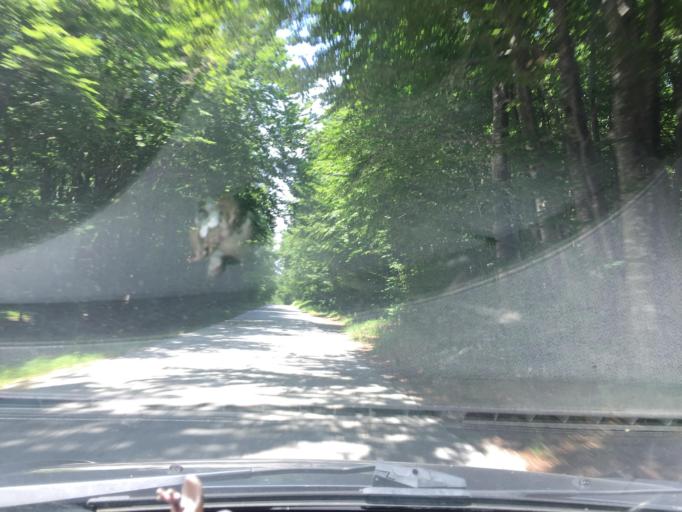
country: HR
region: Istarska
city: Buzet
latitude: 45.4748
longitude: 14.0858
